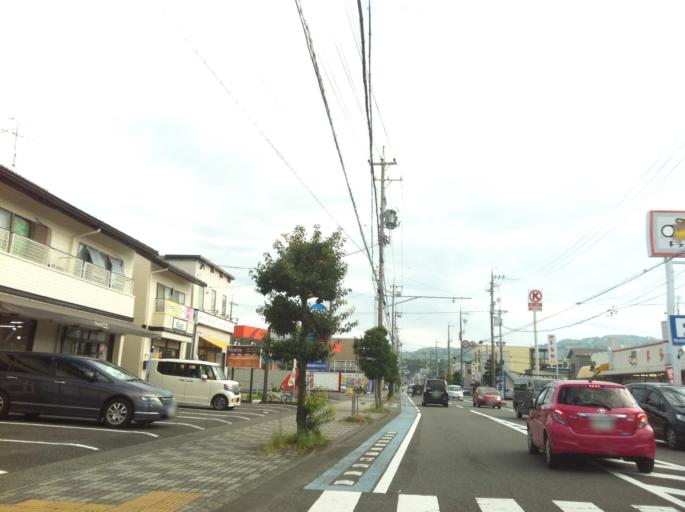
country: JP
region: Shizuoka
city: Shizuoka-shi
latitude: 35.0050
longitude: 138.4818
